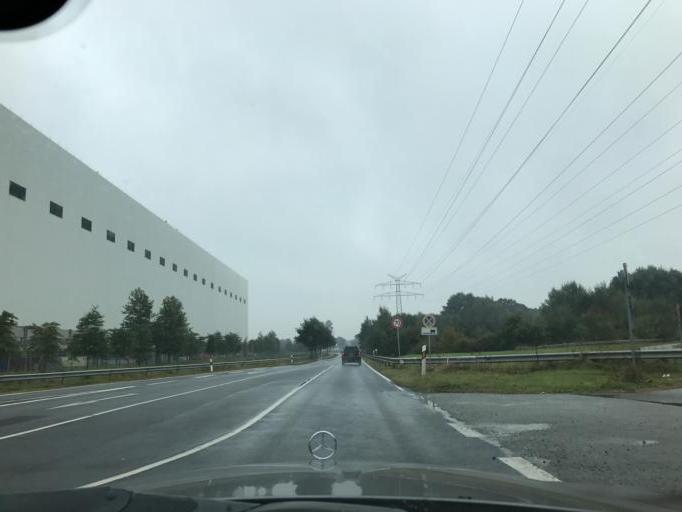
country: DE
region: Lower Saxony
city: Papenburg
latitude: 53.0985
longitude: 7.3544
